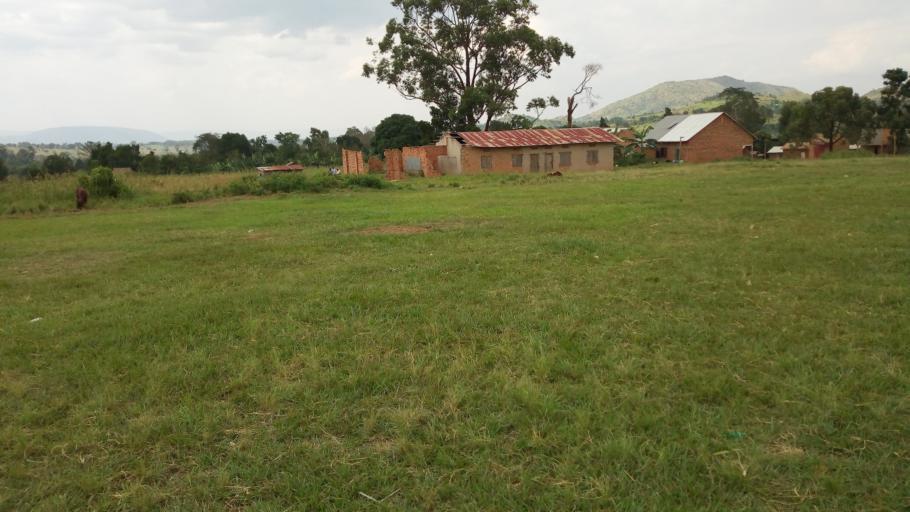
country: UG
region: Central Region
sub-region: Kiboga District
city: Kiboga
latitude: 0.7083
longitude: 31.7648
